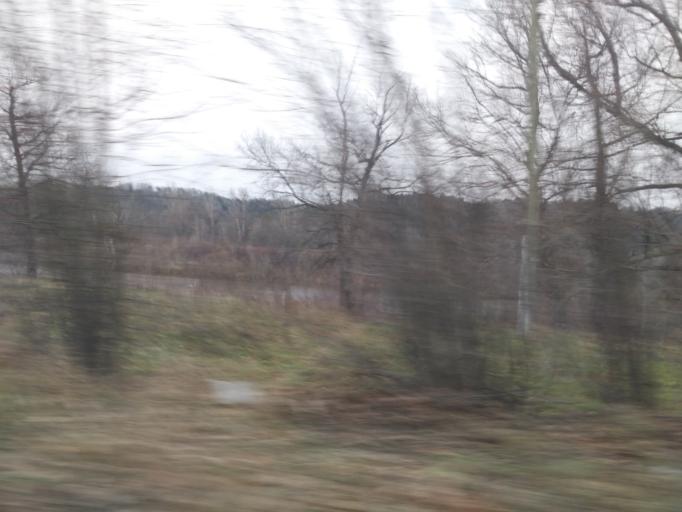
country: RU
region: Kirov
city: Krasnaya Polyana
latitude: 56.2442
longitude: 51.1788
